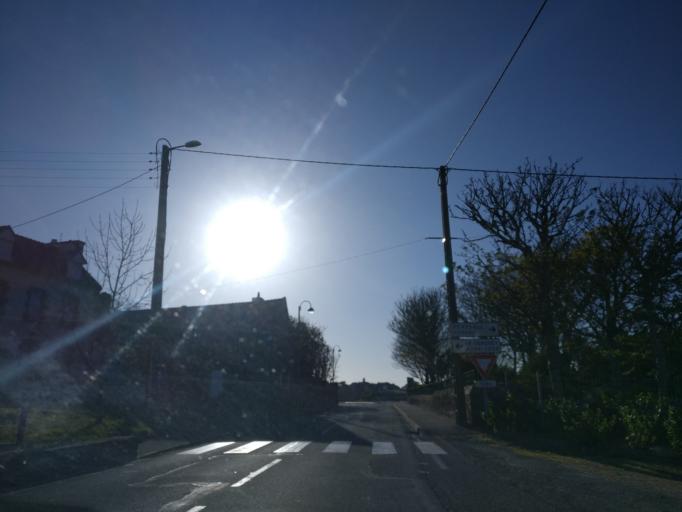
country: FR
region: Brittany
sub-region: Departement du Finistere
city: Porspoder
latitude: 48.5208
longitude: -4.7561
